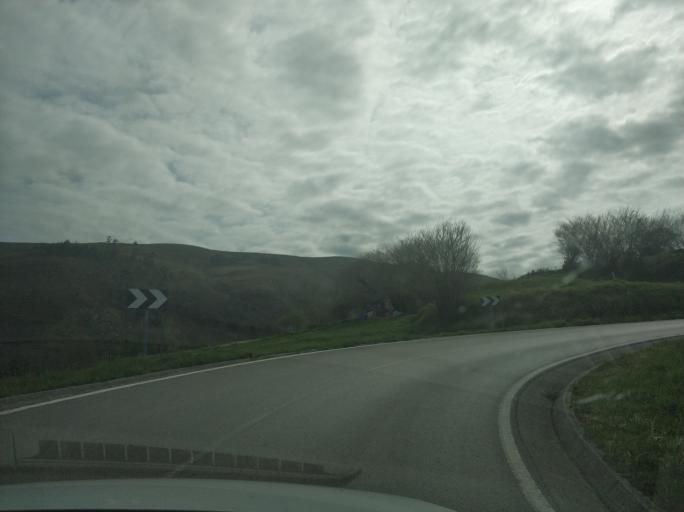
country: ES
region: Cantabria
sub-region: Provincia de Cantabria
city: Ruente
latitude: 43.2380
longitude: -4.2822
